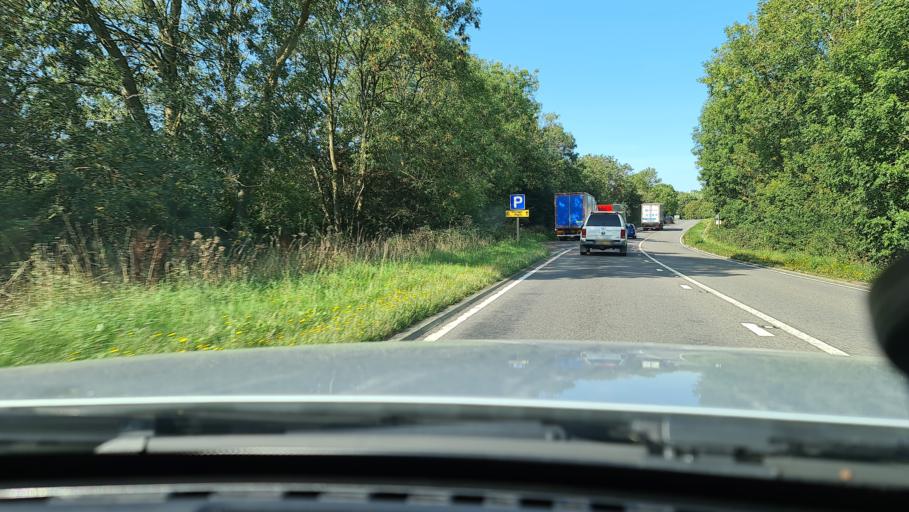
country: GB
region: England
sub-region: Northamptonshire
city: Daventry
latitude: 52.2436
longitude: -1.1388
